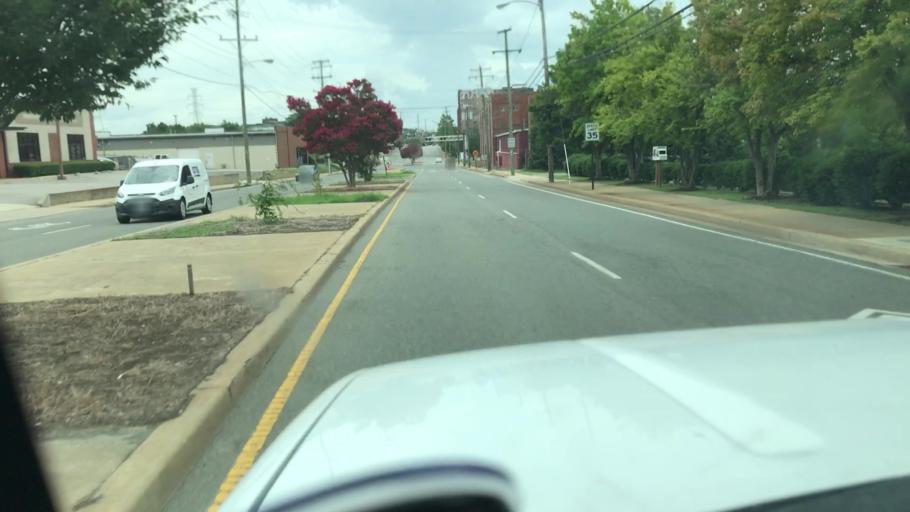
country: US
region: Virginia
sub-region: City of Richmond
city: Richmond
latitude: 37.5652
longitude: -77.4606
